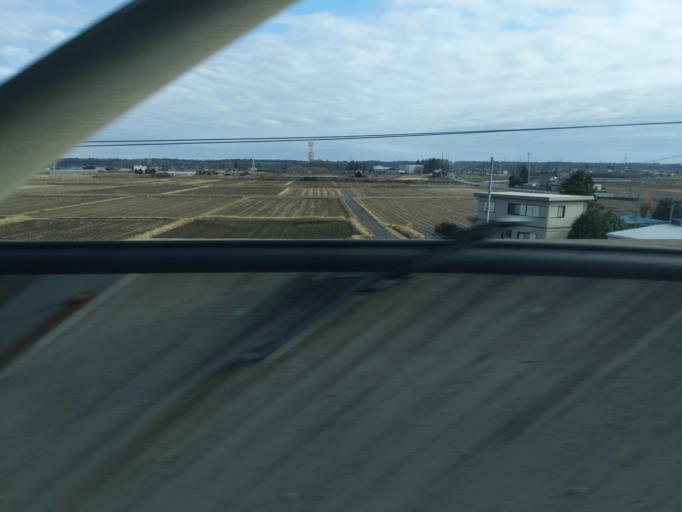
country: JP
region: Tochigi
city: Ujiie
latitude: 36.6366
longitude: 139.9104
